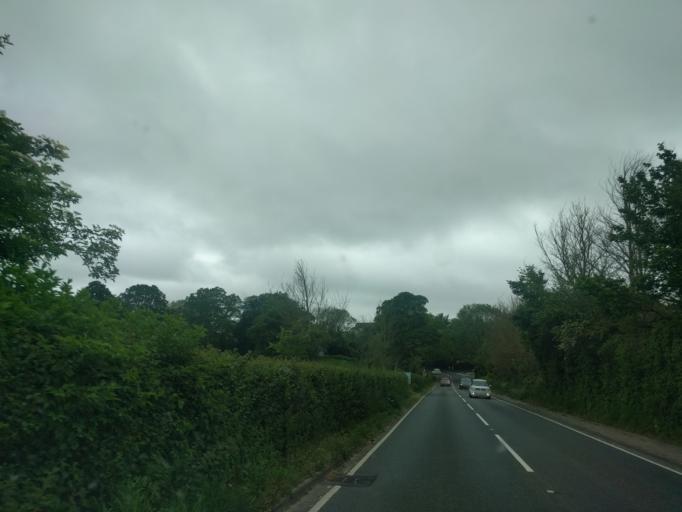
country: GB
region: England
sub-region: Somerset
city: Ilchester
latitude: 51.0571
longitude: -2.7210
